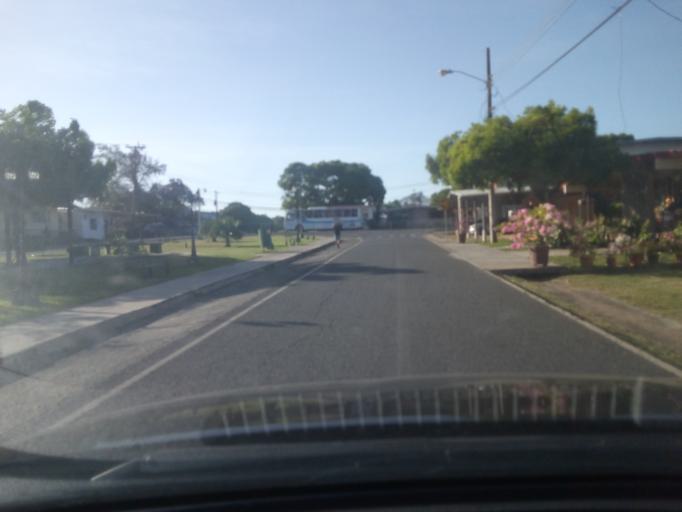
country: PA
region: Veraguas
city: Atalaya
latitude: 8.0442
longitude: -80.9253
